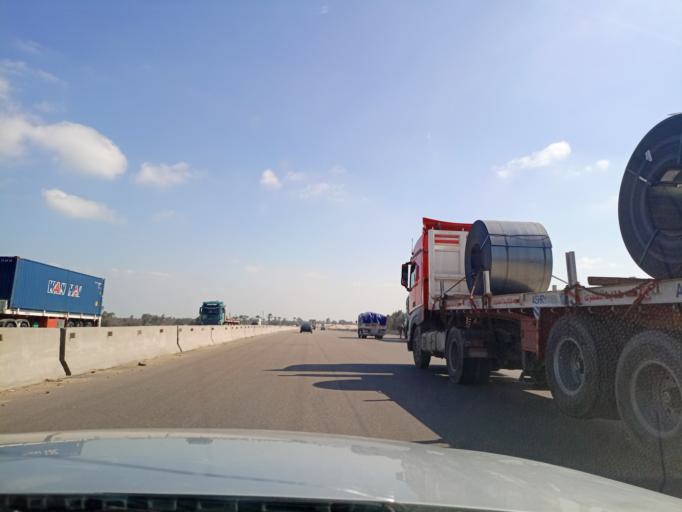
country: EG
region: Eastern Province
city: Mashtul as Suq
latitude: 30.4654
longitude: 31.3072
